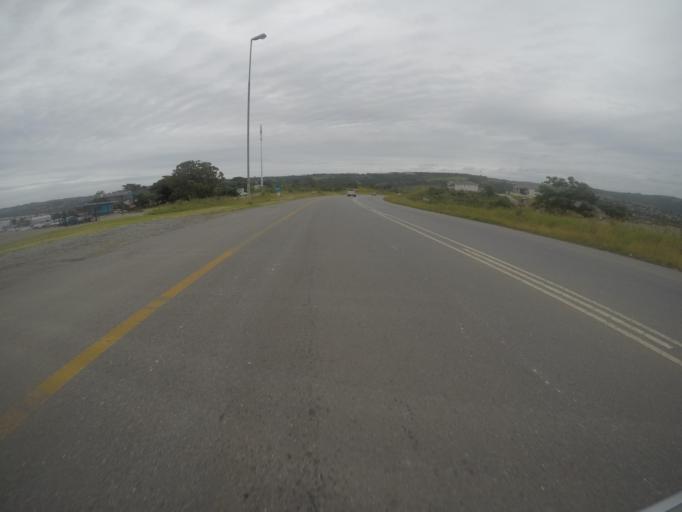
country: ZA
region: Eastern Cape
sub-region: Buffalo City Metropolitan Municipality
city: East London
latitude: -32.9515
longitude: 27.9181
